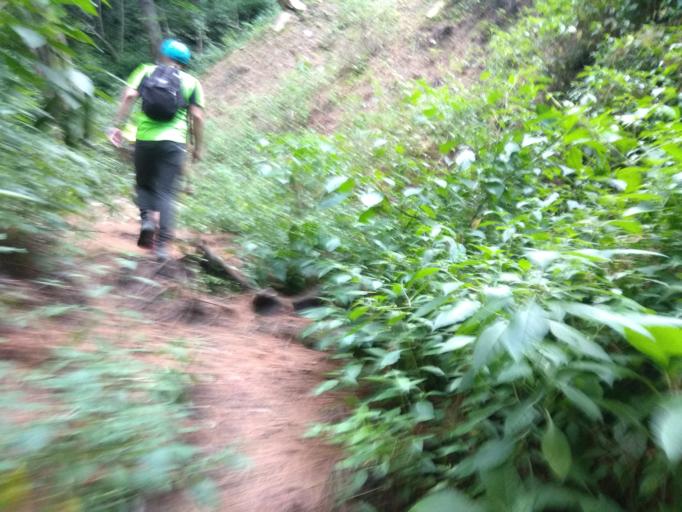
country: CR
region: Cartago
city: Cot
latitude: 9.9596
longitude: -83.8837
